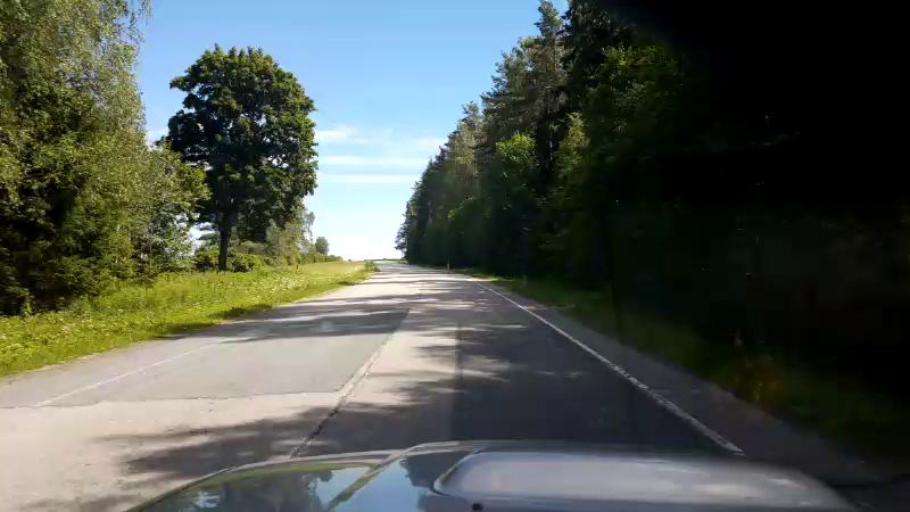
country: EE
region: Jaervamaa
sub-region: Koeru vald
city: Koeru
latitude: 58.9797
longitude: 26.0583
